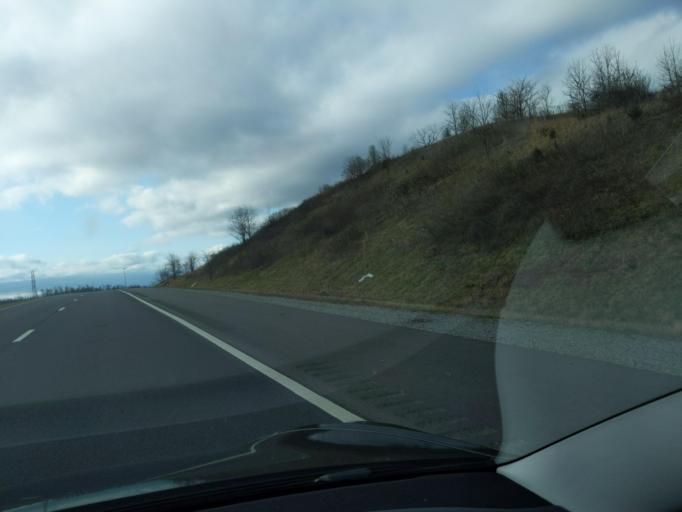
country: US
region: Tennessee
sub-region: Jefferson County
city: White Pine
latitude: 36.1556
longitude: -83.3439
